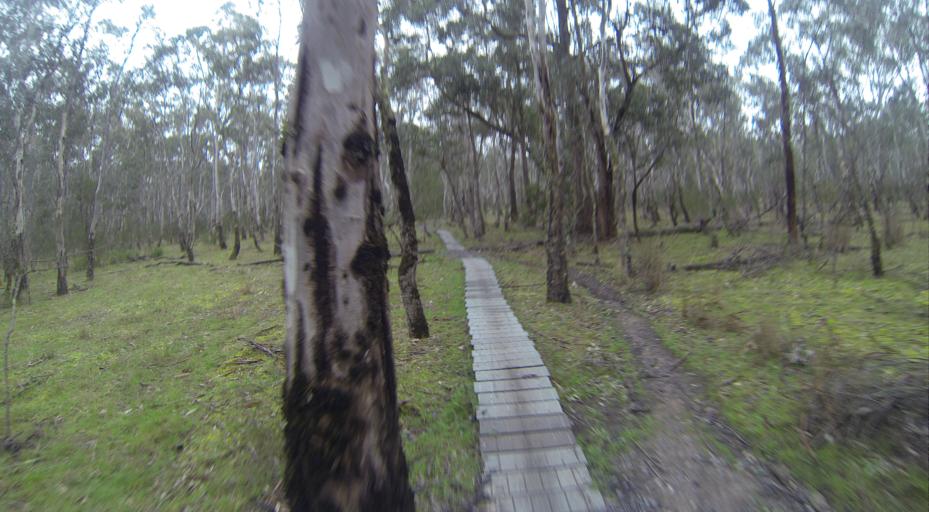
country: AU
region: Victoria
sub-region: Yarra Ranges
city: Lysterfield
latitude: -37.9450
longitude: 145.2939
